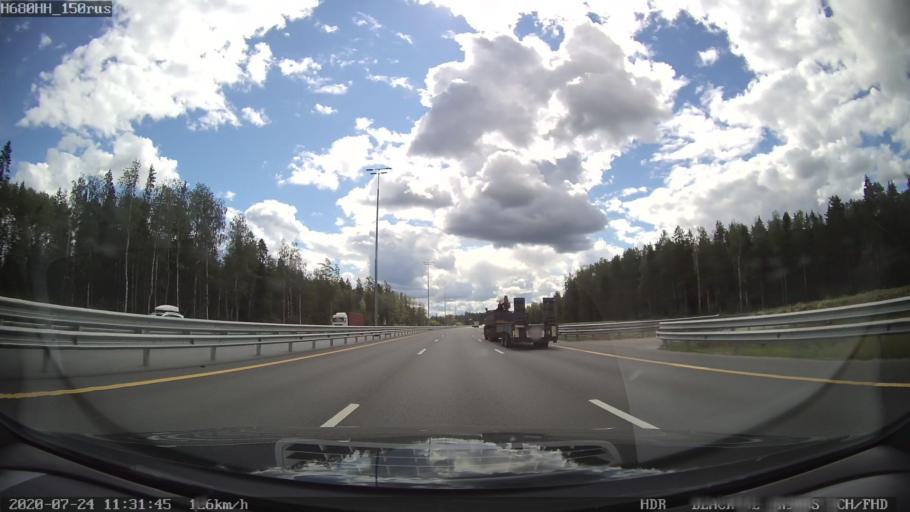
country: RU
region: Leningrad
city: Krasnyy Bor
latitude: 59.6519
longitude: 30.6451
